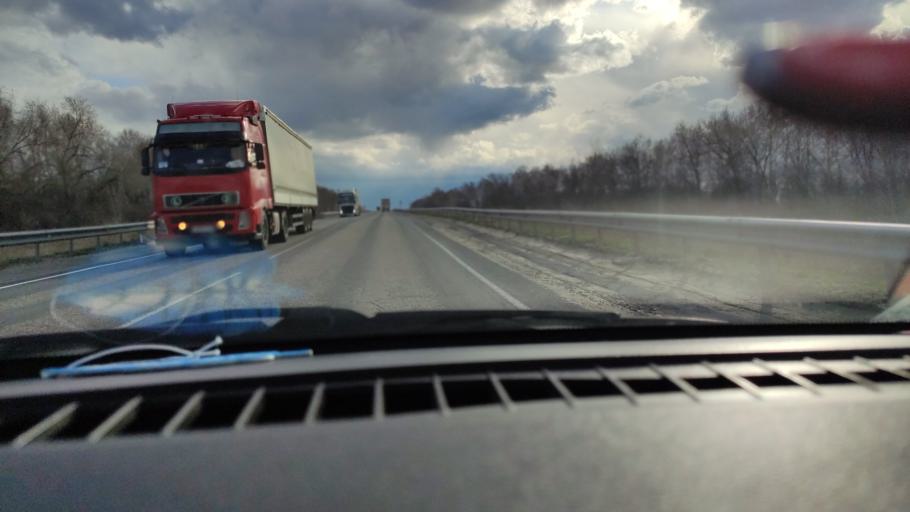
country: RU
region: Saratov
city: Sinodskoye
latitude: 51.9614
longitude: 46.6251
